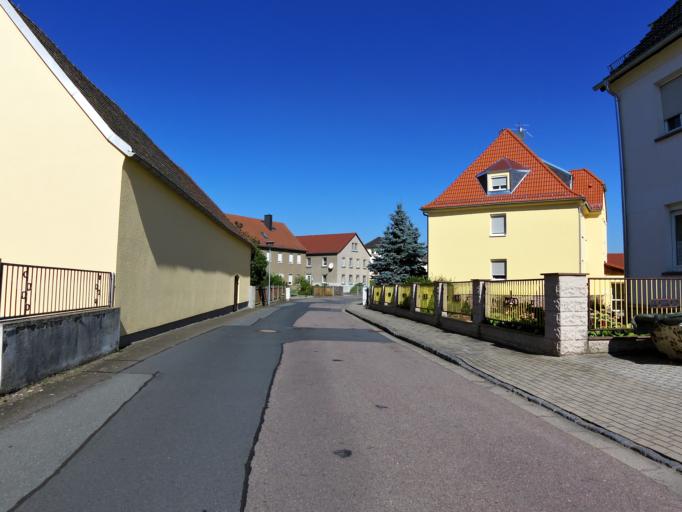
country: DE
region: Saxony
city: Riesa
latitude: 51.3251
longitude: 13.2984
